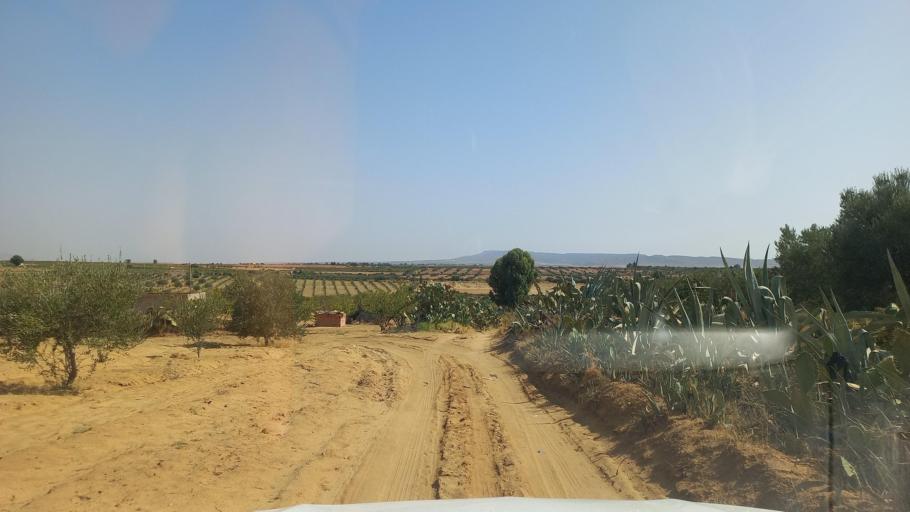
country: TN
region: Al Qasrayn
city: Kasserine
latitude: 35.2363
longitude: 9.0552
